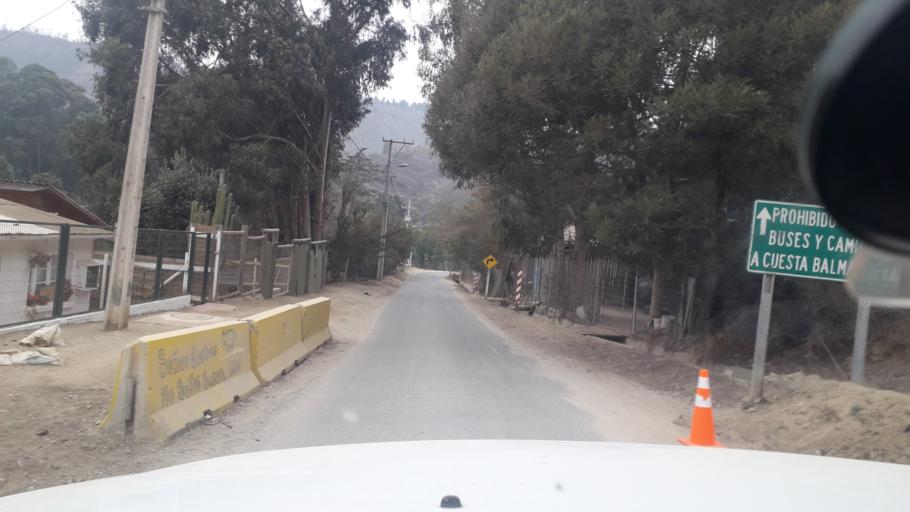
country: CL
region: Valparaiso
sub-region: Provincia de Valparaiso
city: Valparaiso
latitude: -33.1065
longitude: -71.6654
